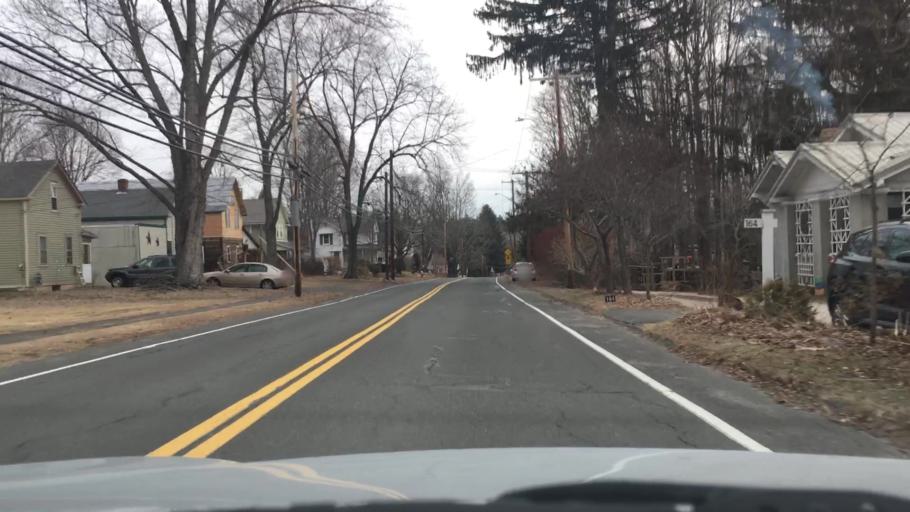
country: US
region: Massachusetts
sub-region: Hampshire County
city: Northampton
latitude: 42.3234
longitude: -72.6588
